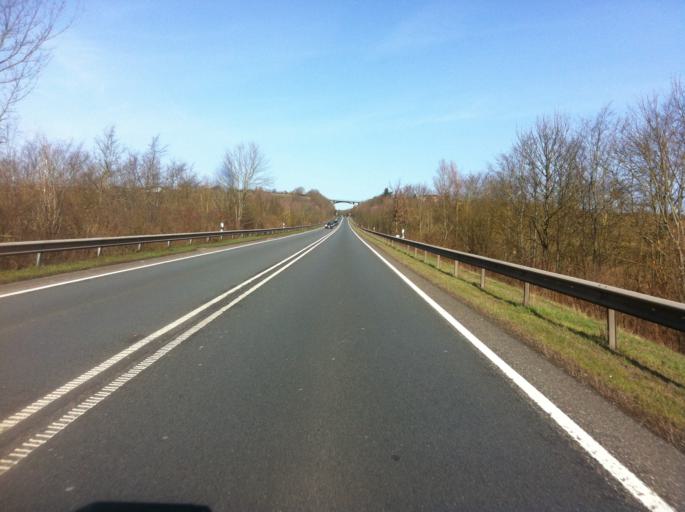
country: DE
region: Rheinland-Pfalz
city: Mendig
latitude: 50.3618
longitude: 7.2694
